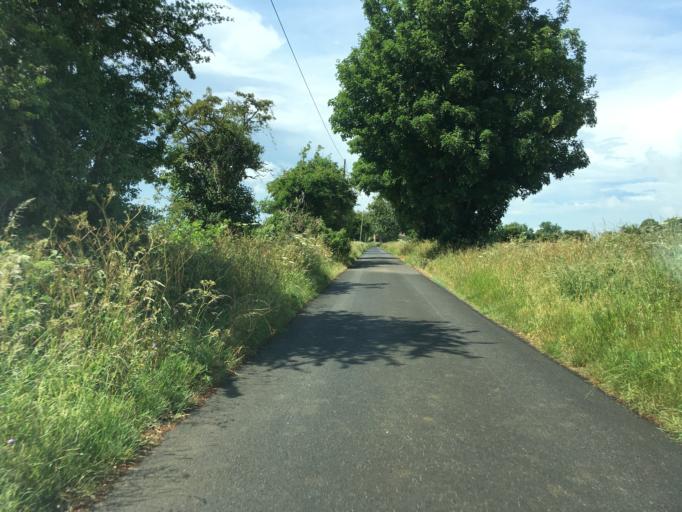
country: GB
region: England
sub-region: Gloucestershire
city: Tetbury
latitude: 51.6280
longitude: -2.2061
